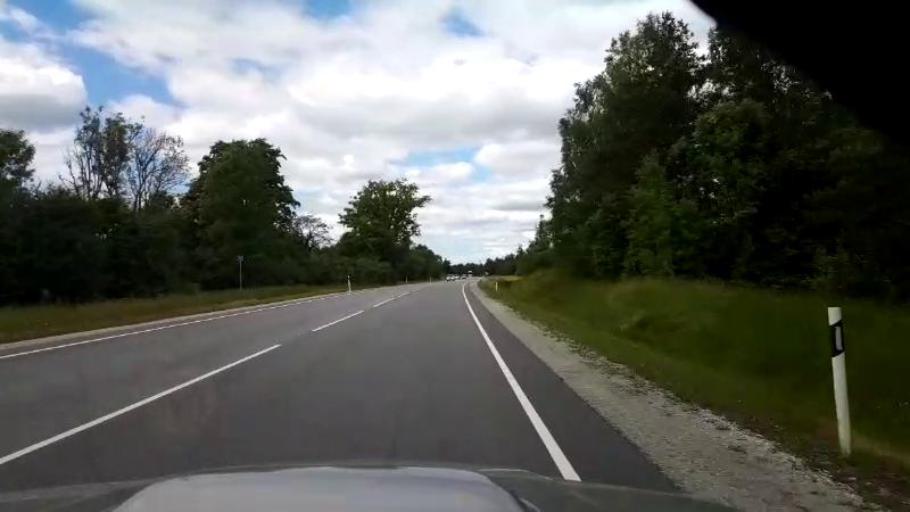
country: EE
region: Raplamaa
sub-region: Maerjamaa vald
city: Marjamaa
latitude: 58.9713
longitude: 24.4758
